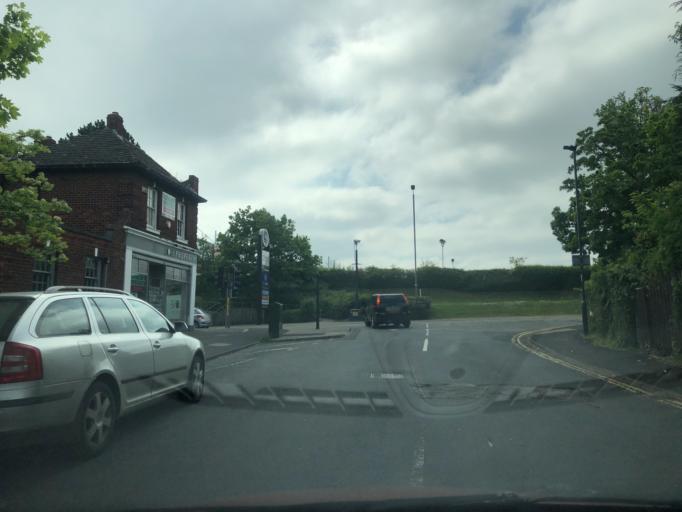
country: GB
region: England
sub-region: North Yorkshire
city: Catterick Garrison
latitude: 54.3755
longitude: -1.7212
